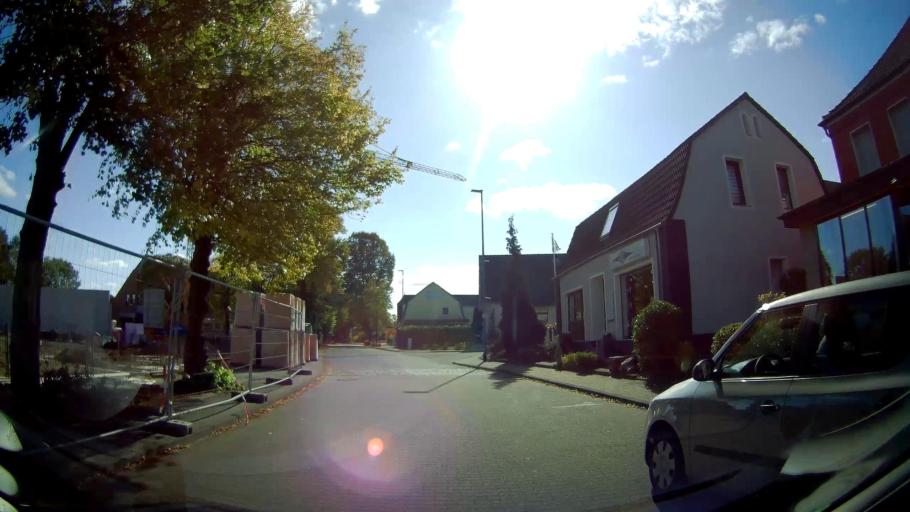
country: DE
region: North Rhine-Westphalia
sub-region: Regierungsbezirk Dusseldorf
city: Hunxe
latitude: 51.6419
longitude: 6.7656
